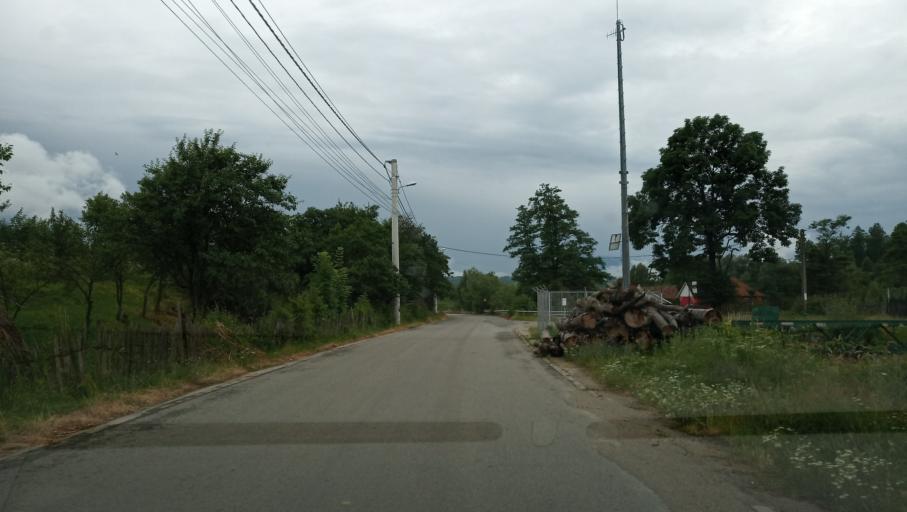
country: RO
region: Hunedoara
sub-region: Oras Petrila
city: Petrila
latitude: 45.4589
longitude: 23.4191
